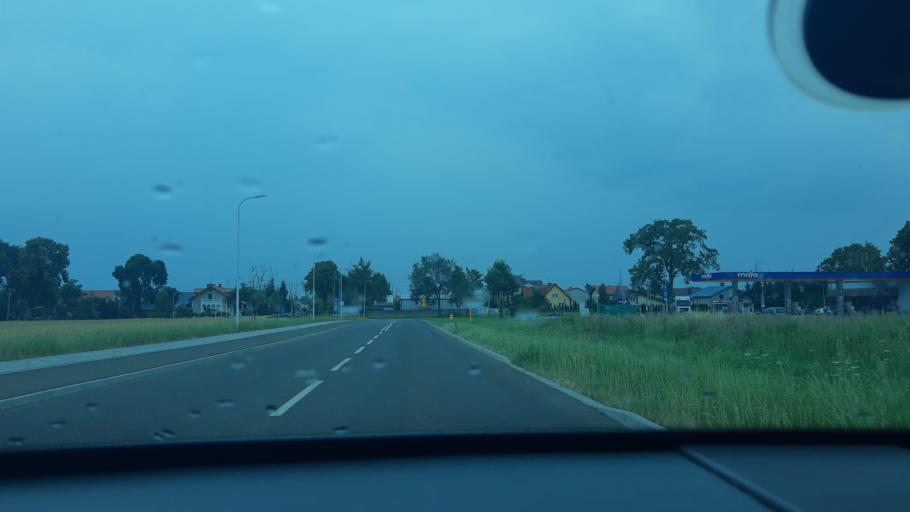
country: PL
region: Lodz Voivodeship
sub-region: Powiat sieradzki
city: Sieradz
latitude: 51.5721
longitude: 18.7025
